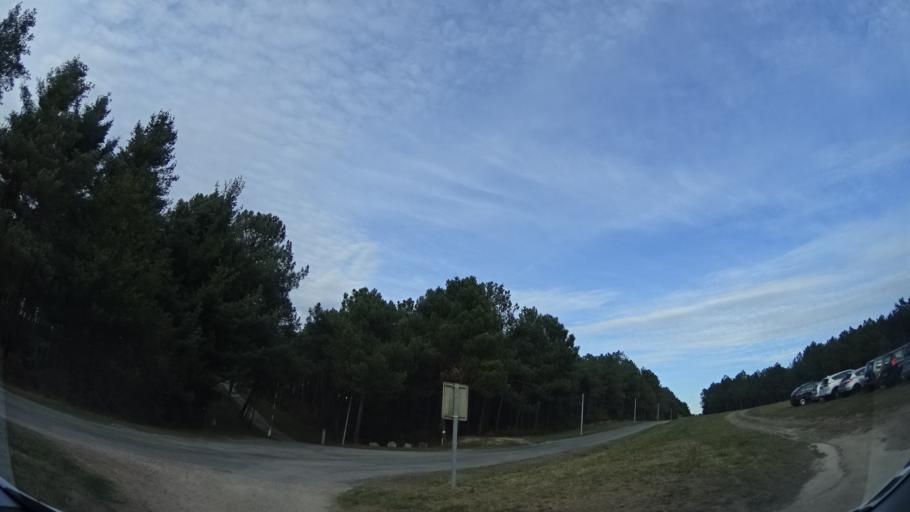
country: FR
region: Brittany
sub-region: Departement d'Ille-et-Vilaine
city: Iffendic
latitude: 48.0961
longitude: -2.0542
